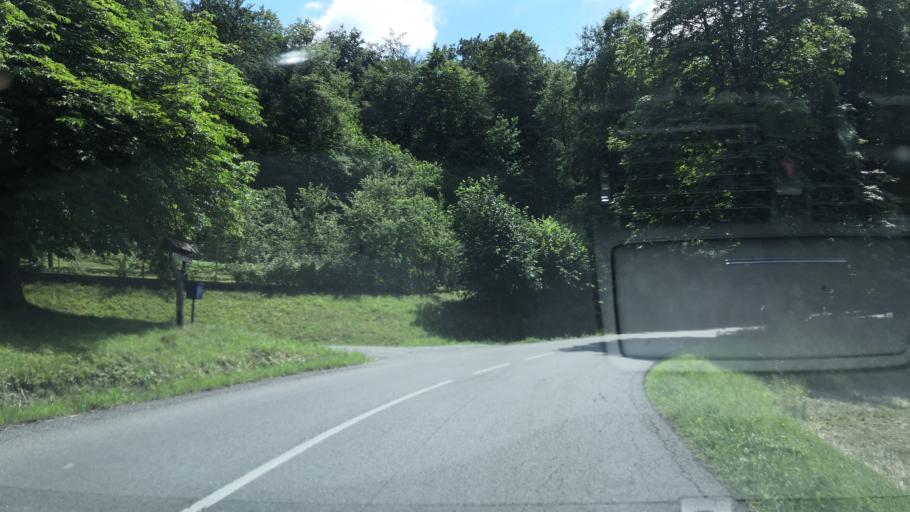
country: CZ
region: Zlin
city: Valasska Bystrice
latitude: 49.4303
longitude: 18.1292
